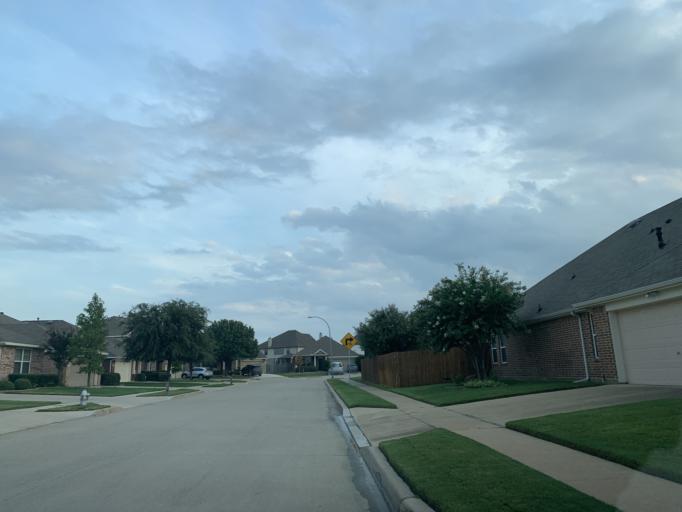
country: US
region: Texas
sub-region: Tarrant County
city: Keller
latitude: 32.9228
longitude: -97.2733
